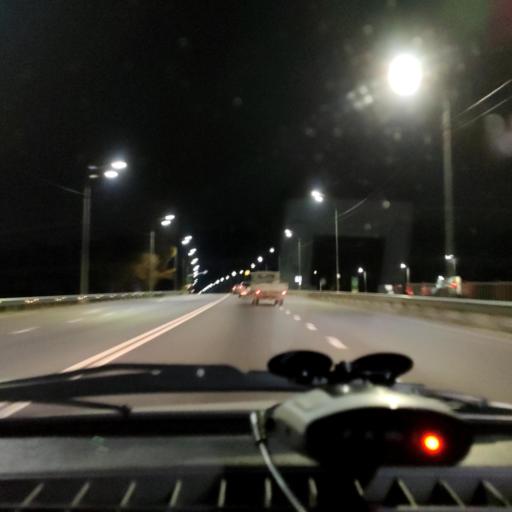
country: RU
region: Voronezj
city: Semiluki
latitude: 51.6501
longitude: 39.0323
